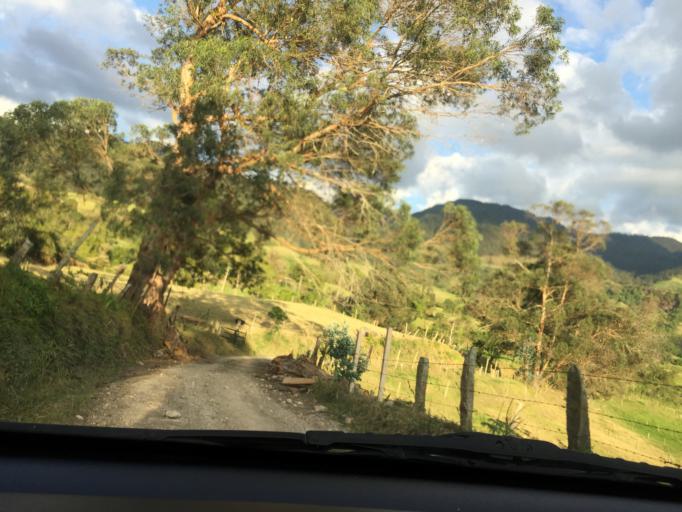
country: CO
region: Cundinamarca
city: Zipacon
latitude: 4.7283
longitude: -74.3907
